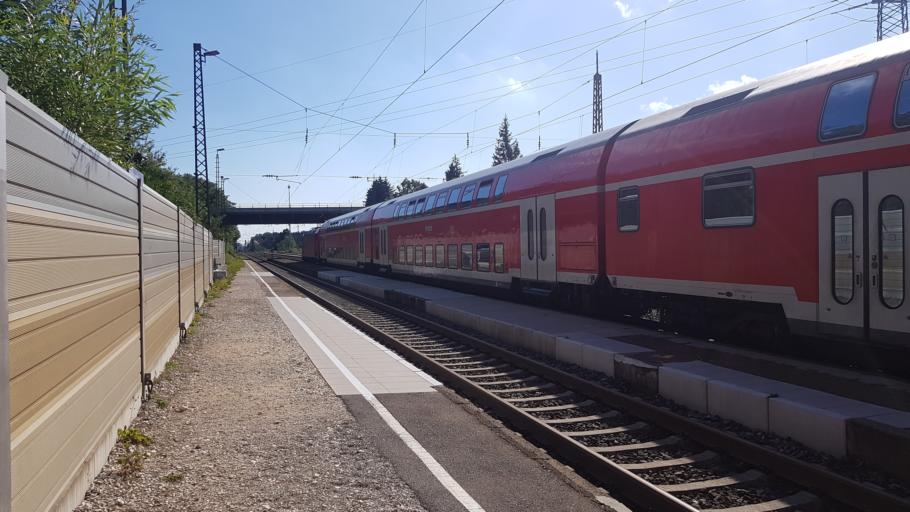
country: DE
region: Baden-Wuerttemberg
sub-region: Tuebingen Region
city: Beimerstetten
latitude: 48.4813
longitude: 9.9770
